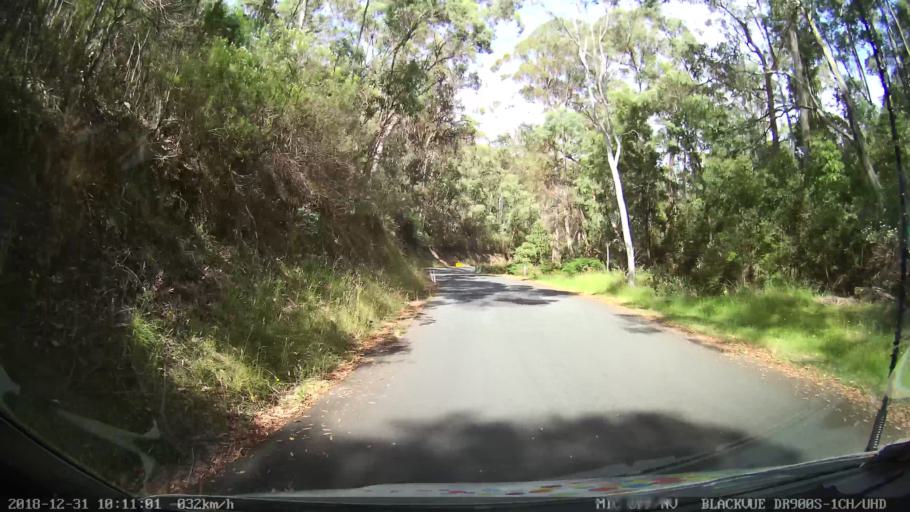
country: AU
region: New South Wales
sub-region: Snowy River
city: Jindabyne
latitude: -36.5384
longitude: 148.1693
